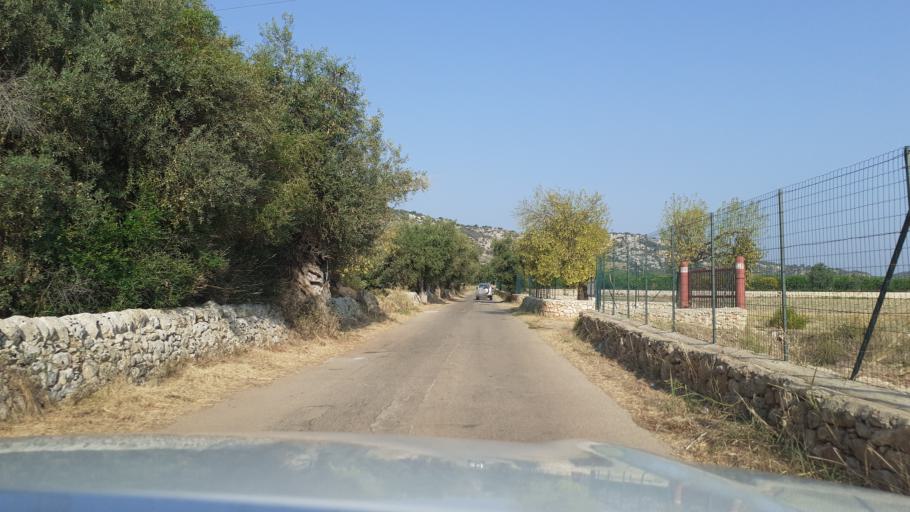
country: IT
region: Sicily
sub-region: Provincia di Siracusa
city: Cassibile
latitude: 36.9759
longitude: 15.1830
